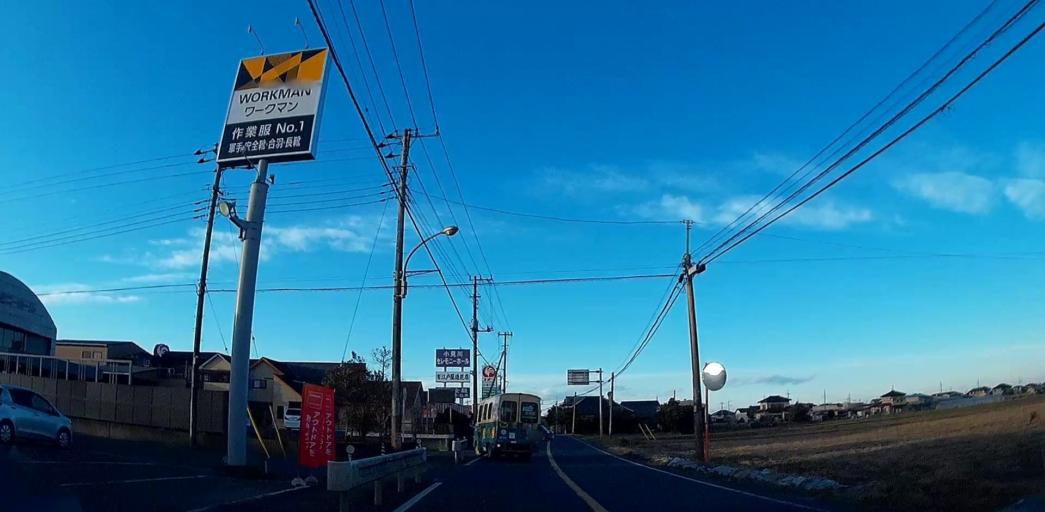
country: JP
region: Chiba
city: Omigawa
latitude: 35.8624
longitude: 140.5978
